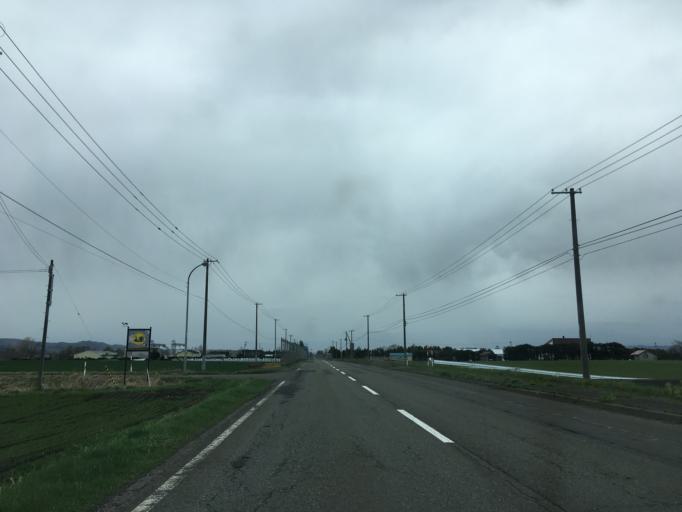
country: JP
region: Hokkaido
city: Chitose
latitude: 42.9278
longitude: 141.8075
